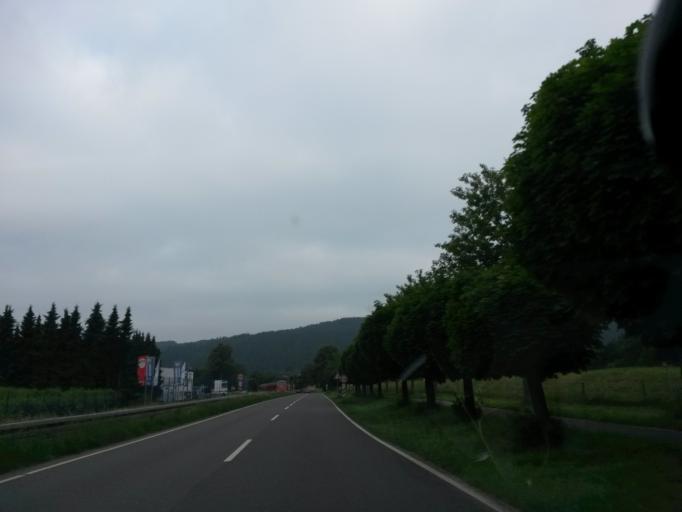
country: DE
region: North Rhine-Westphalia
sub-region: Regierungsbezirk Koln
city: Engelskirchen
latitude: 50.9760
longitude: 7.3547
